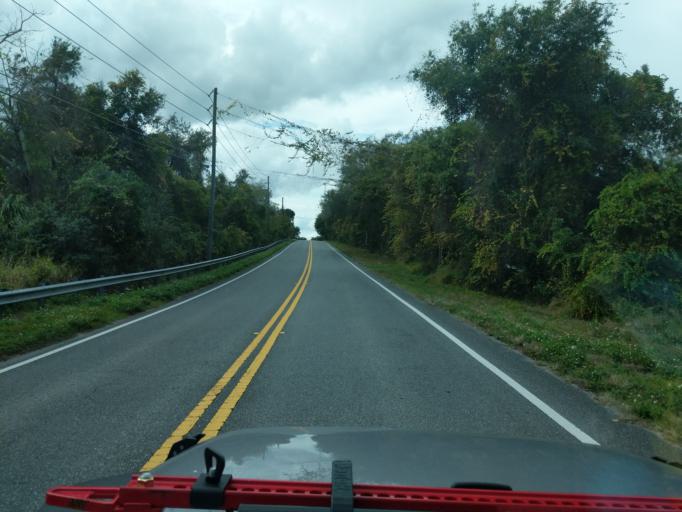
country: US
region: Florida
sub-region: Lake County
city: Groveland
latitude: 28.5685
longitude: -81.8107
